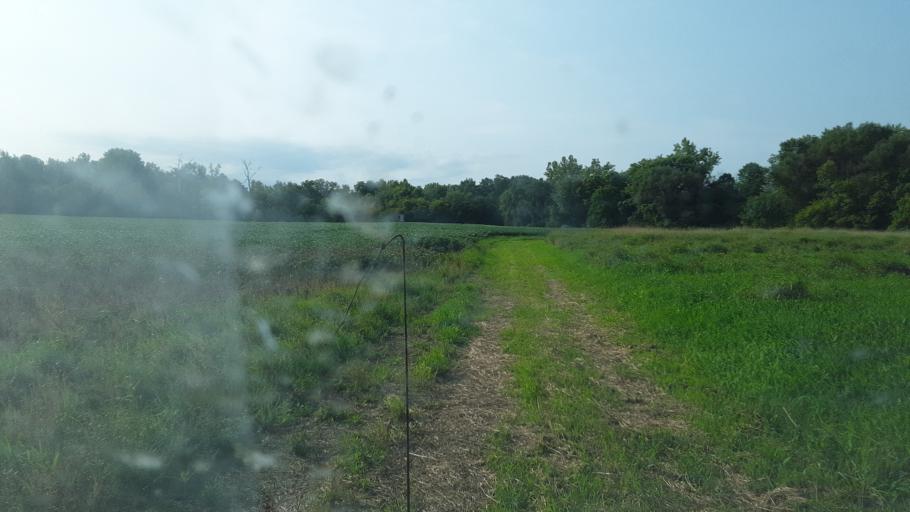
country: US
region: Ohio
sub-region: Crawford County
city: Bucyrus
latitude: 40.6616
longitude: -82.9552
